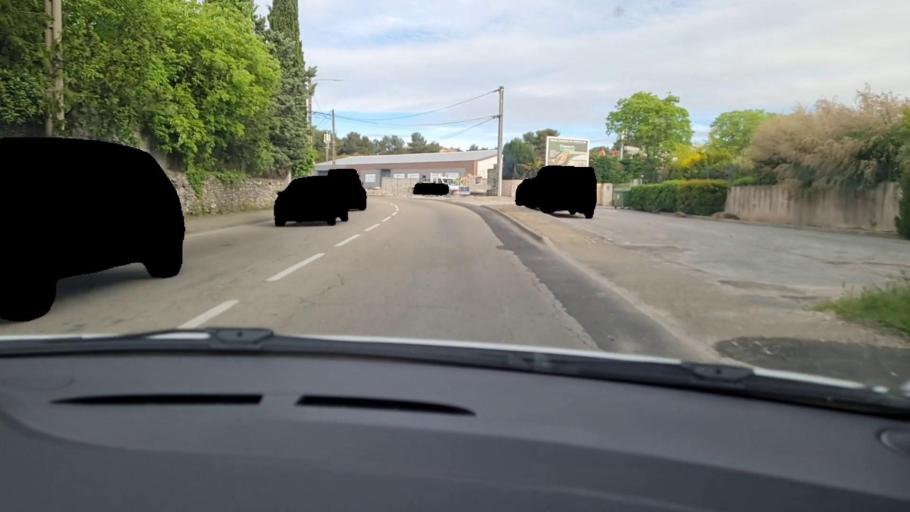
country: FR
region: Languedoc-Roussillon
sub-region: Departement du Gard
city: Nimes
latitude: 43.8421
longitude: 4.3131
